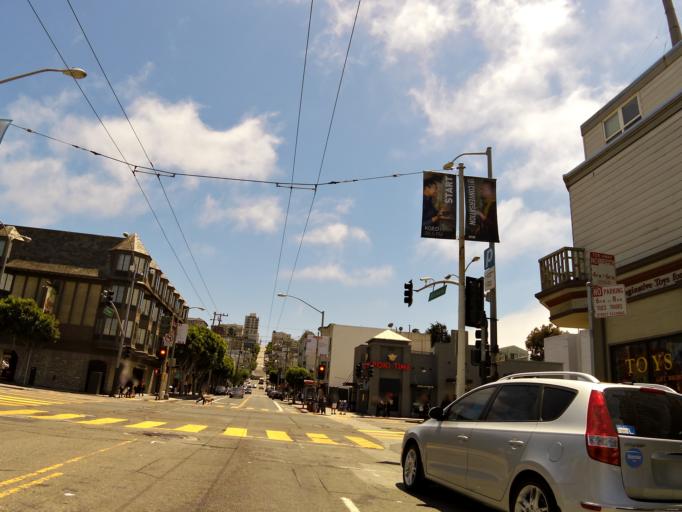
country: US
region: California
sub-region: San Francisco County
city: San Francisco
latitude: 37.8001
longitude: -122.4362
